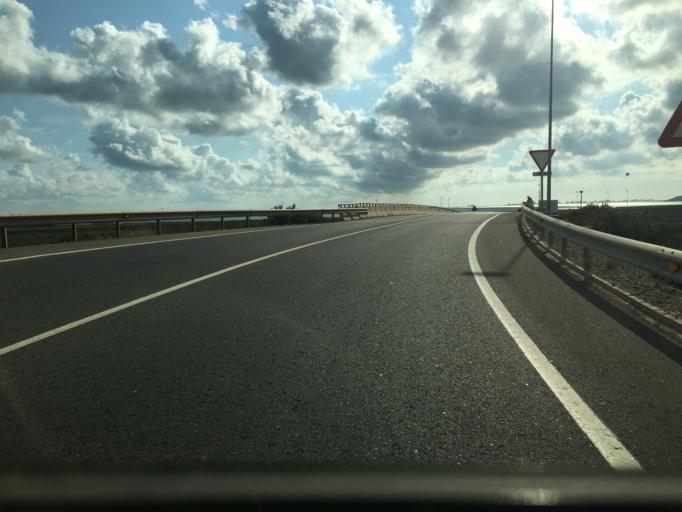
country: ES
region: Murcia
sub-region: Murcia
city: Los Alcazares
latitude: 37.7044
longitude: -0.8665
